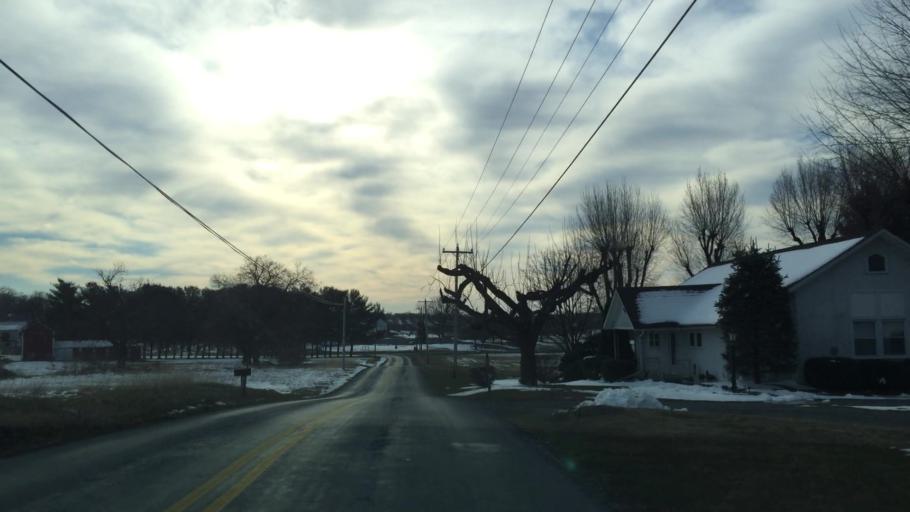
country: US
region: Virginia
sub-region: City of Winchester
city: Winchester
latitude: 39.2543
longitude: -78.1370
